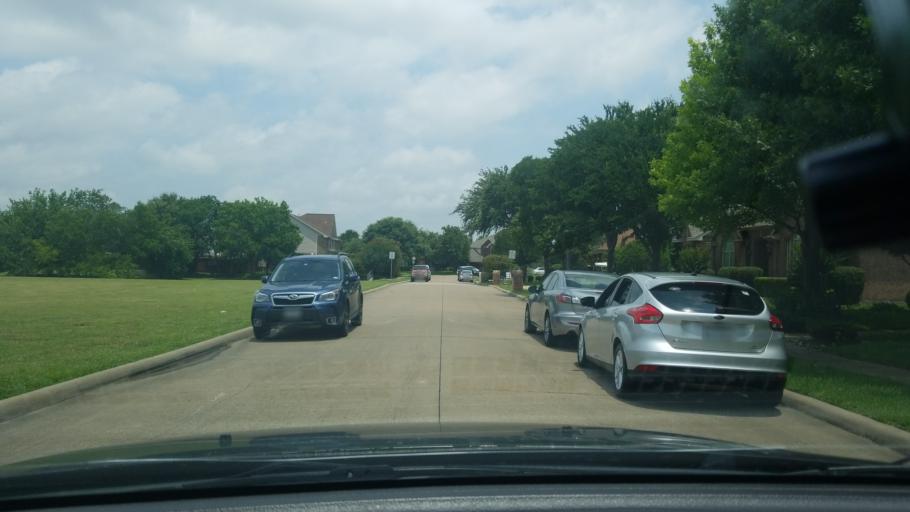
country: US
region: Texas
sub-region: Dallas County
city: Sunnyvale
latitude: 32.8103
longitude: -96.6020
